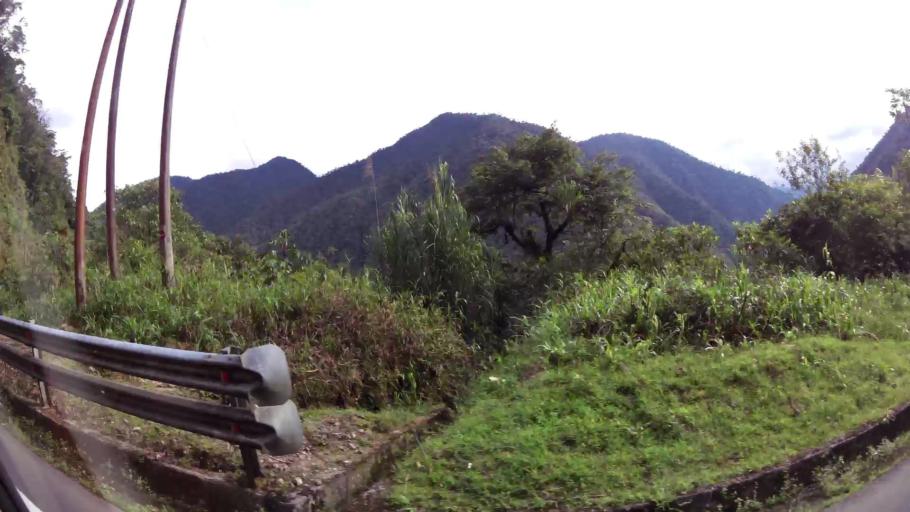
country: EC
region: Pastaza
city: Puyo
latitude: -1.4450
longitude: -78.1770
